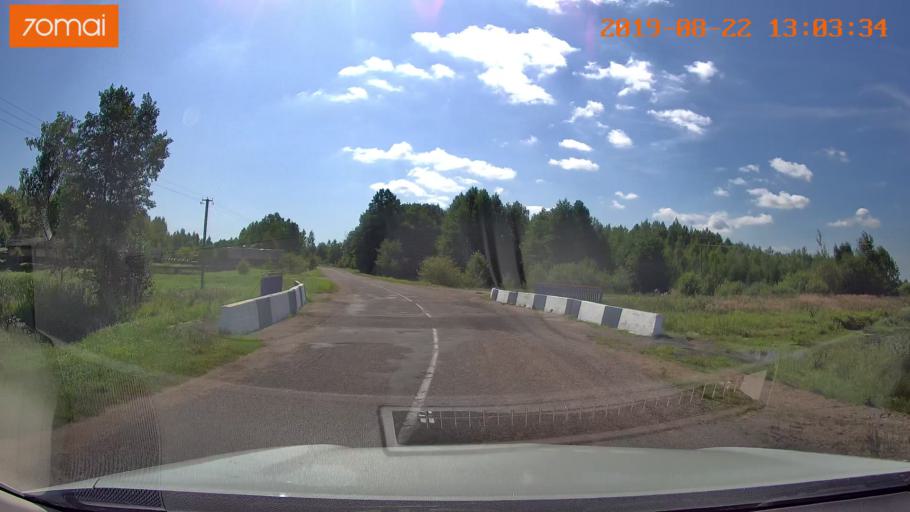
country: BY
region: Minsk
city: Prawdzinski
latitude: 53.3793
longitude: 27.8206
